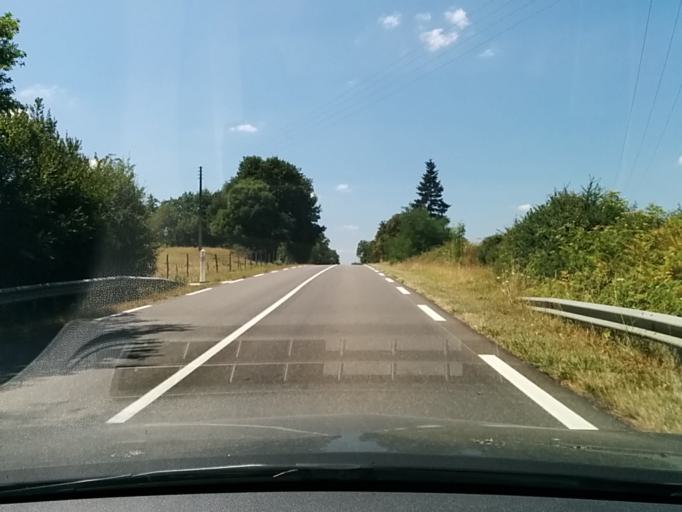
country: FR
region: Midi-Pyrenees
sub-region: Departement du Gers
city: Eauze
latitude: 43.7971
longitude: 0.0593
